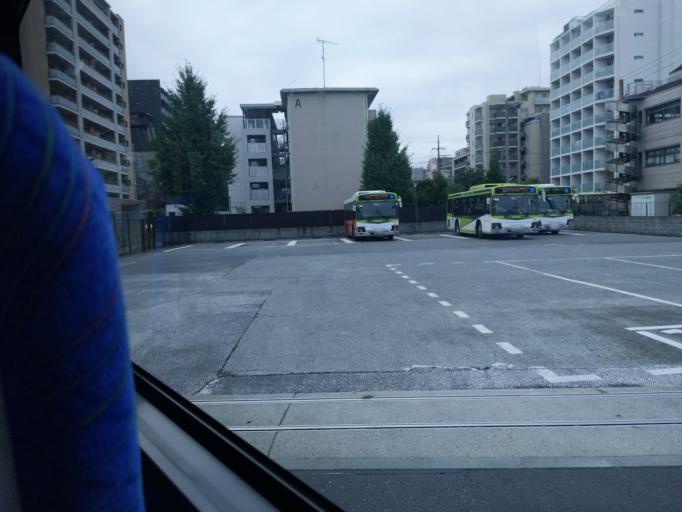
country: JP
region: Saitama
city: Shimotoda
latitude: 35.7909
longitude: 139.6678
